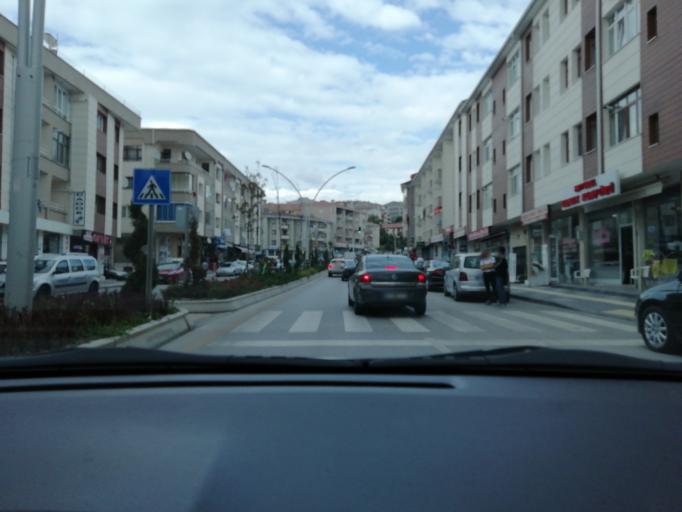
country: TR
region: Ankara
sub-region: Goelbasi
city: Golbasi
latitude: 39.7913
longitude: 32.8113
